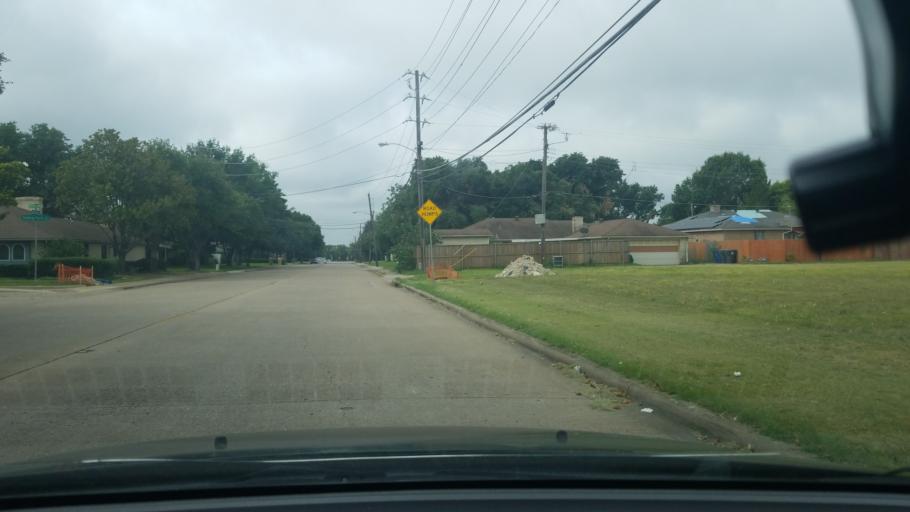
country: US
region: Texas
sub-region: Dallas County
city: Balch Springs
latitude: 32.7914
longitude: -96.6913
